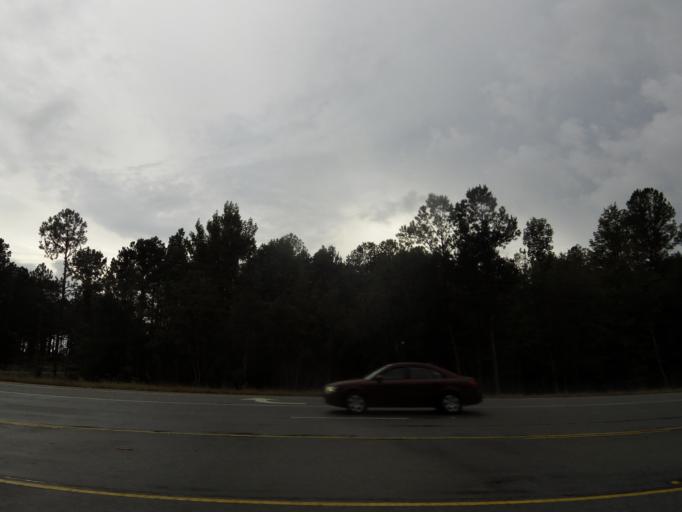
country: US
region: Georgia
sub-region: Wayne County
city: Jesup
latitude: 31.5643
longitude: -81.8371
